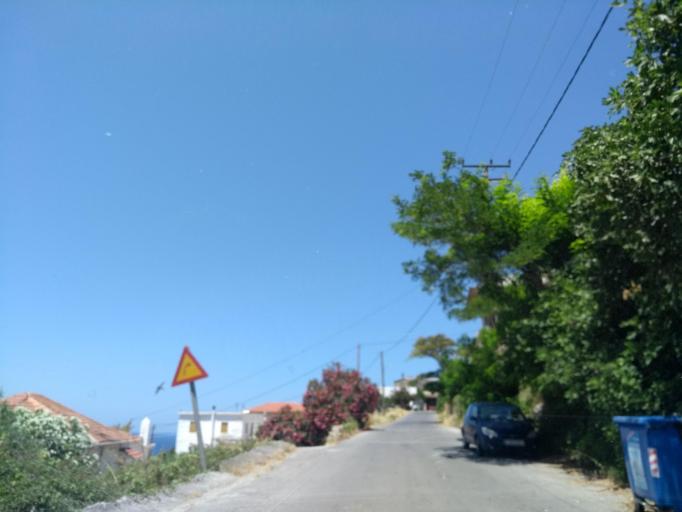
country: GR
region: Crete
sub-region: Nomos Chanias
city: Georgioupolis
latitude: 35.3273
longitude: 24.3346
